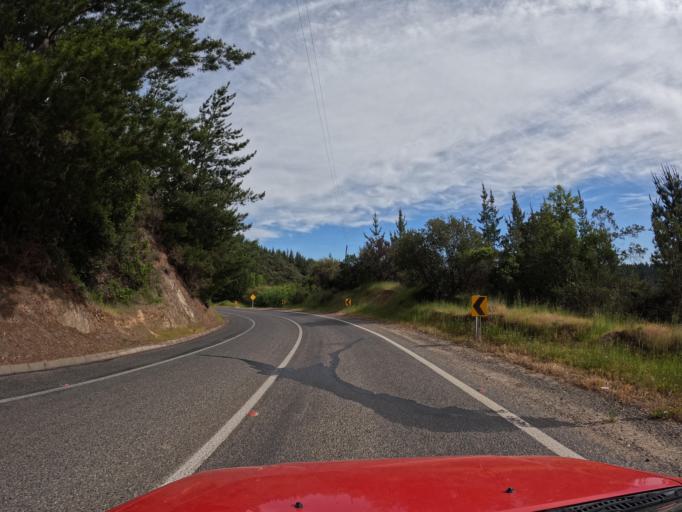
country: CL
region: Maule
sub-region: Provincia de Talca
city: Talca
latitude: -35.2991
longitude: -71.9625
